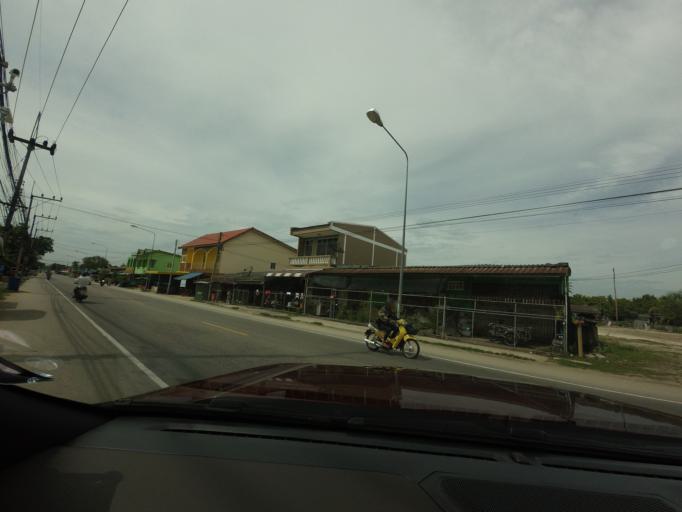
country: TH
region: Narathiwat
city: Tak Bai
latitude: 6.2548
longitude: 102.0604
